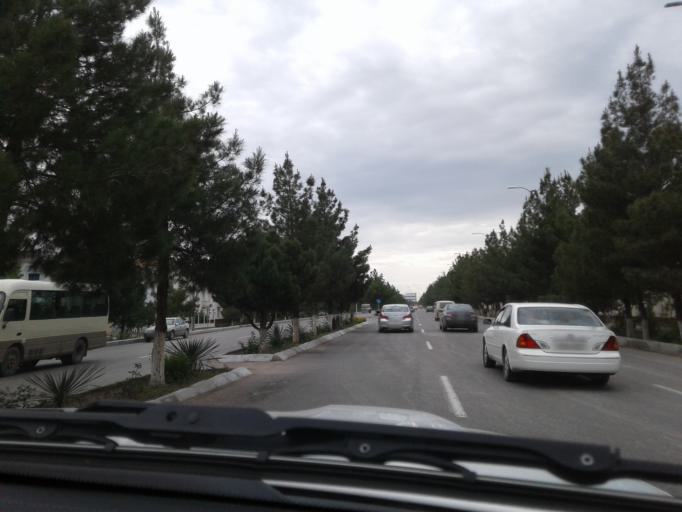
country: TM
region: Mary
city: Mary
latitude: 37.5891
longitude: 61.8667
